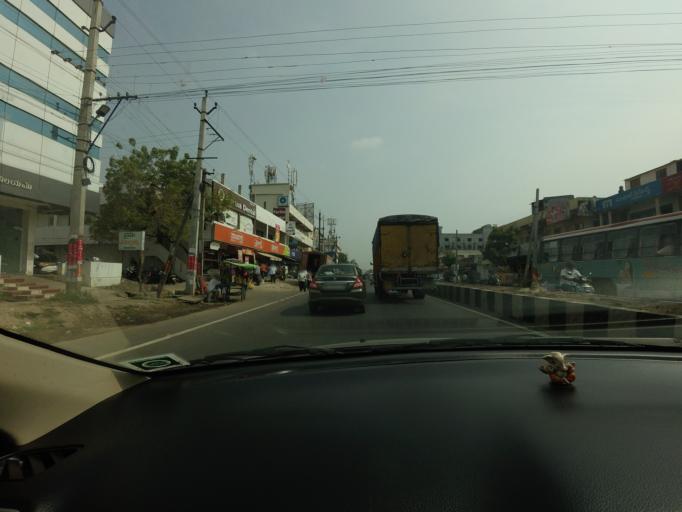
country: IN
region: Andhra Pradesh
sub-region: Krishna
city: Yanamalakuduru
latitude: 16.4876
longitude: 80.6776
